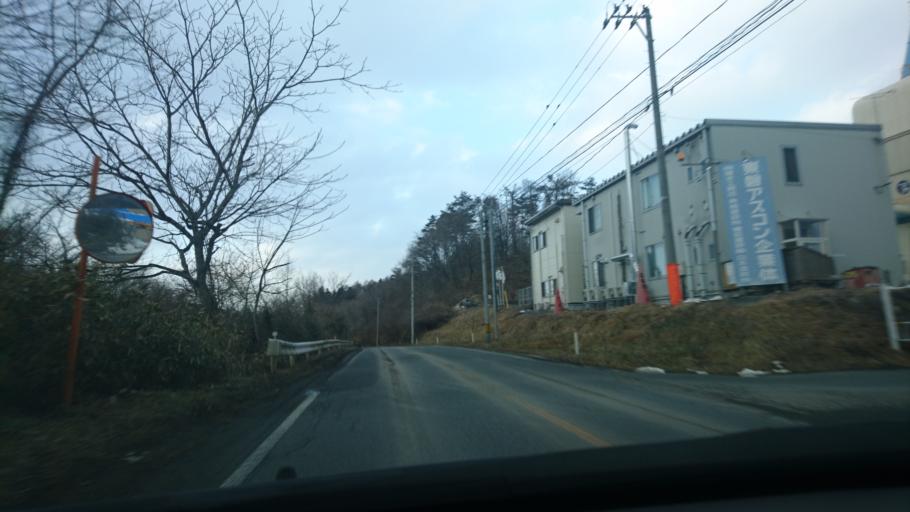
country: JP
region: Iwate
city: Ichinoseki
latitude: 38.9680
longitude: 141.3321
